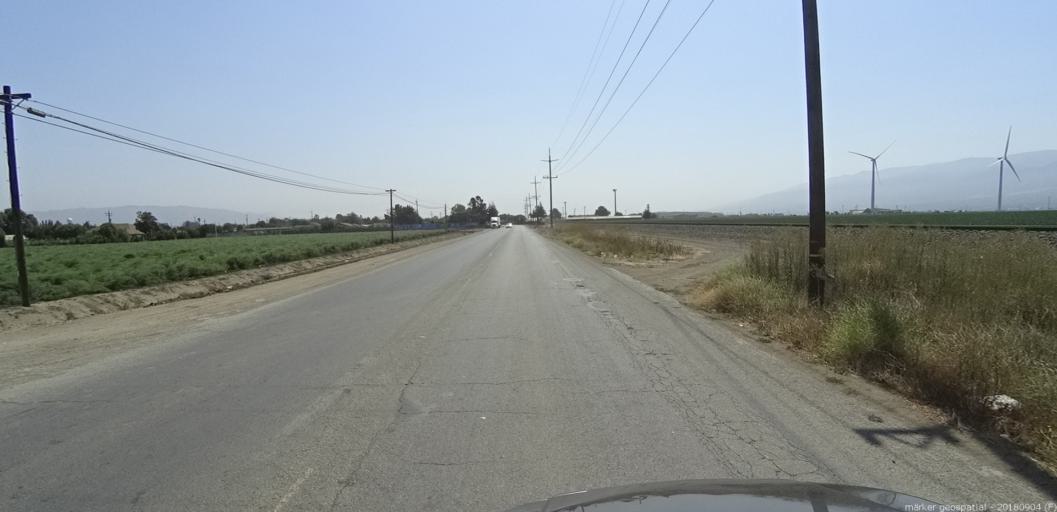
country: US
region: California
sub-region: Monterey County
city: Gonzales
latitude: 36.5130
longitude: -121.4531
